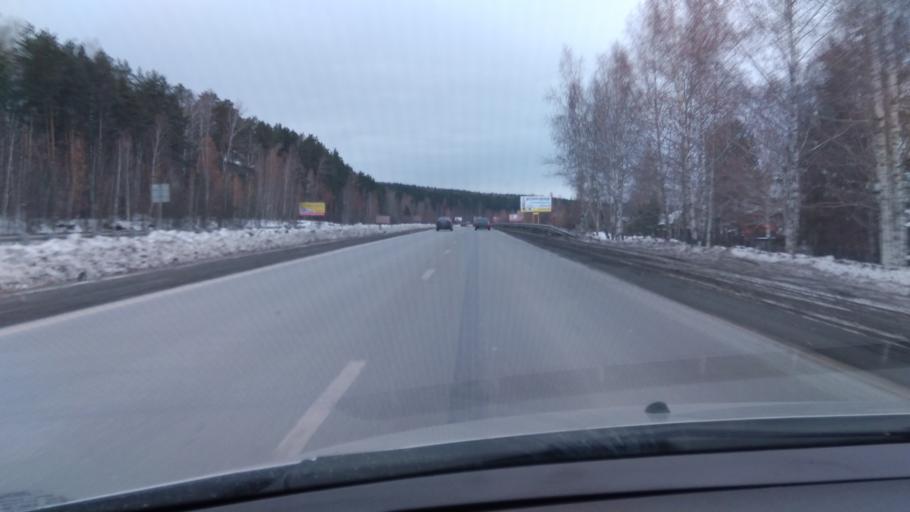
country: RU
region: Sverdlovsk
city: Istok
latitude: 56.7124
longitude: 60.7292
